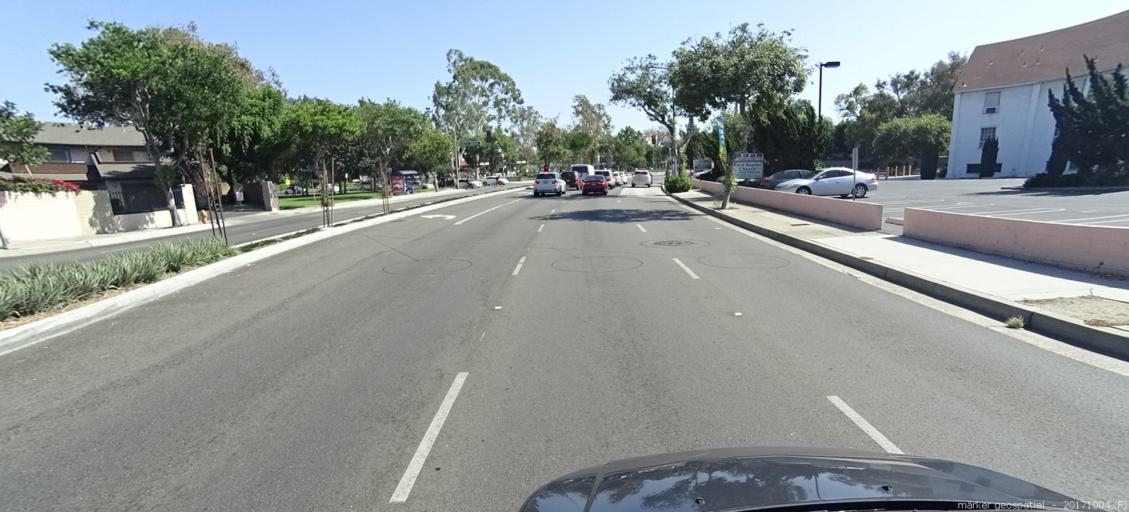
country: US
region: California
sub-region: Orange County
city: Garden Grove
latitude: 33.7780
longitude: -117.9391
